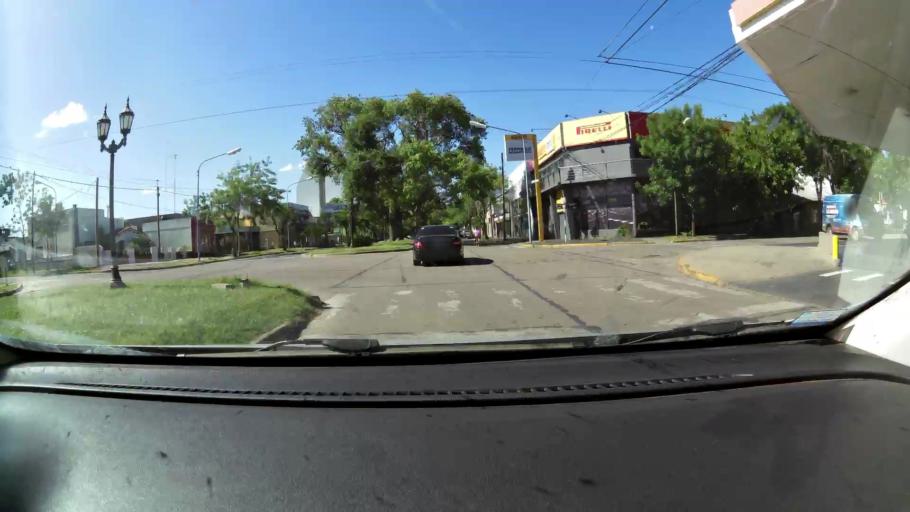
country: AR
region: Santa Fe
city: Rafaela
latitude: -31.2611
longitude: -61.4936
